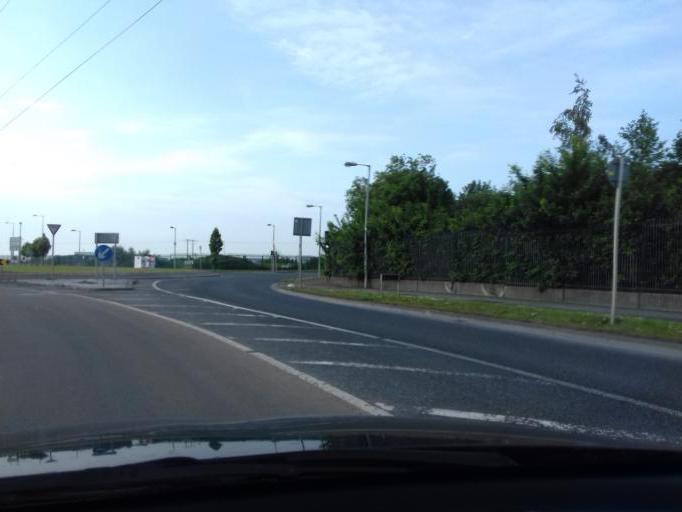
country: IE
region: Leinster
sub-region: Fingal County
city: Blanchardstown
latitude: 53.4119
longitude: -6.3451
